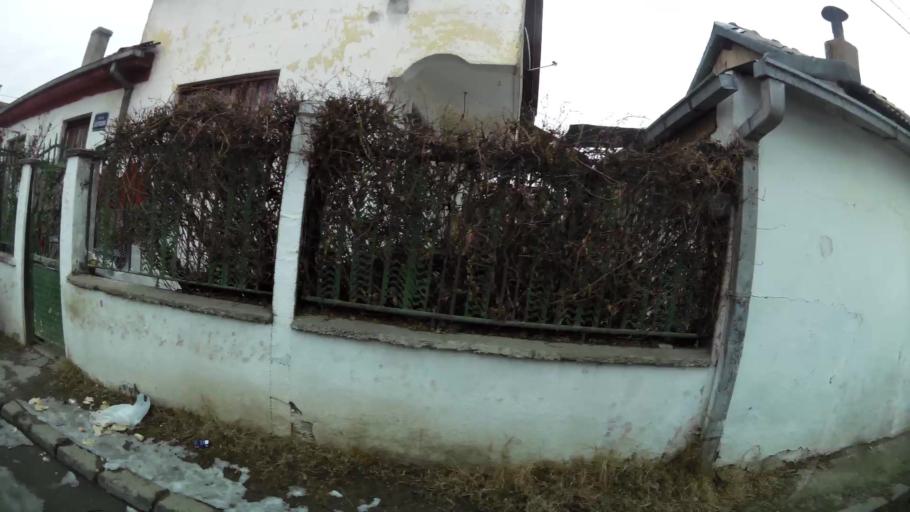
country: MK
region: Suto Orizari
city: Suto Orizare
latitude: 42.0392
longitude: 21.4218
